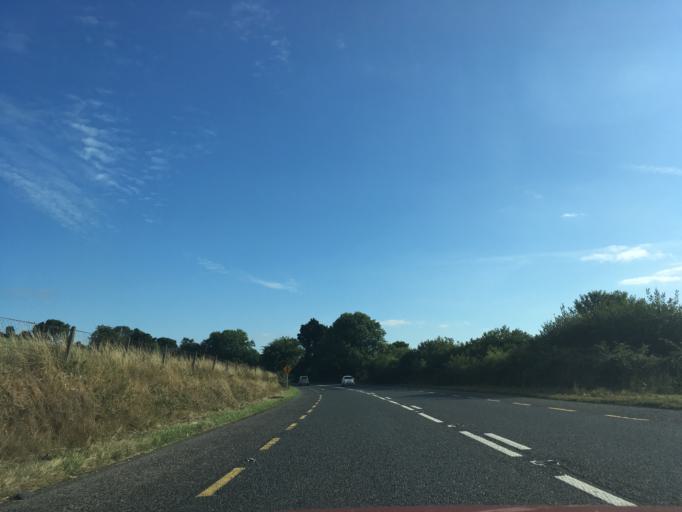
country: IE
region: Munster
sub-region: Waterford
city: Waterford
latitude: 52.3367
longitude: -7.0551
